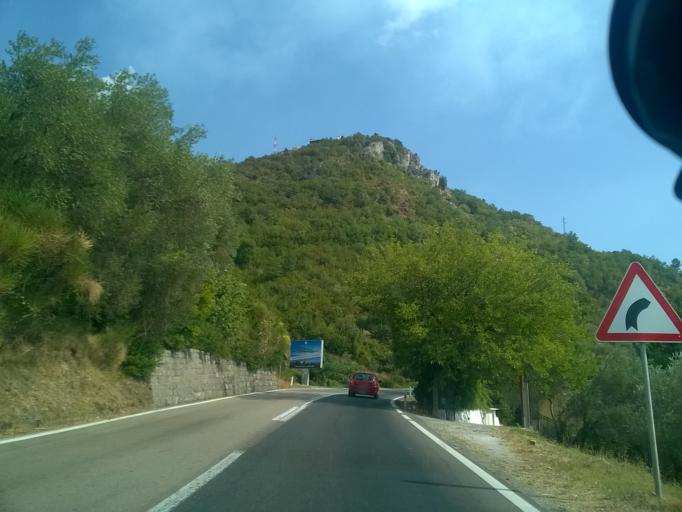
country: ME
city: Petrovac na Moru
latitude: 42.2549
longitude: 18.9001
